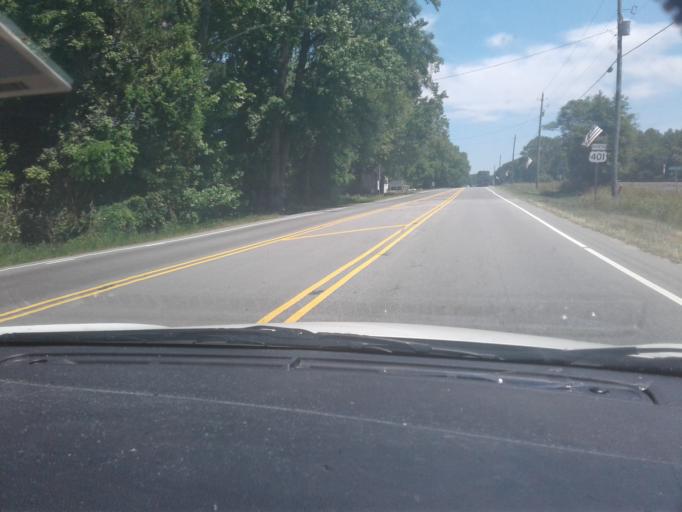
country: US
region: North Carolina
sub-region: Harnett County
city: Lillington
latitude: 35.4804
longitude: -78.8202
